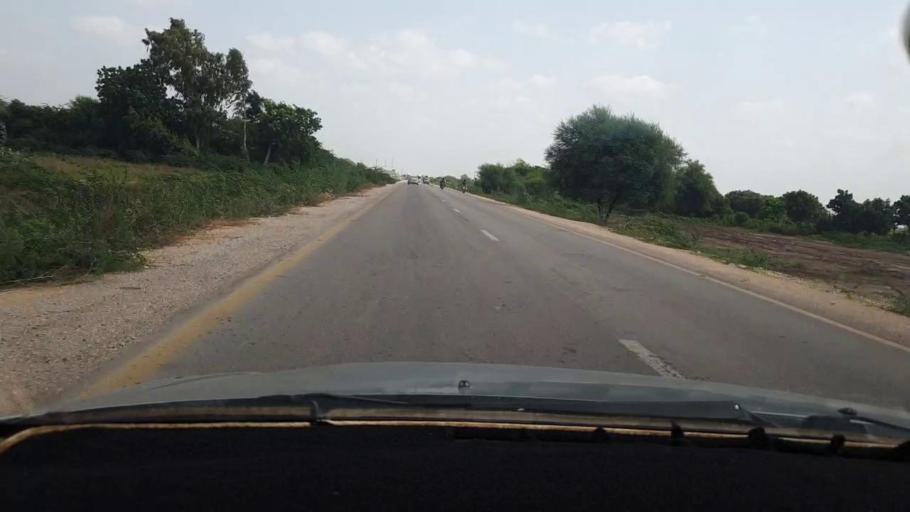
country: PK
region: Sindh
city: Digri
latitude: 25.0914
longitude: 69.1939
